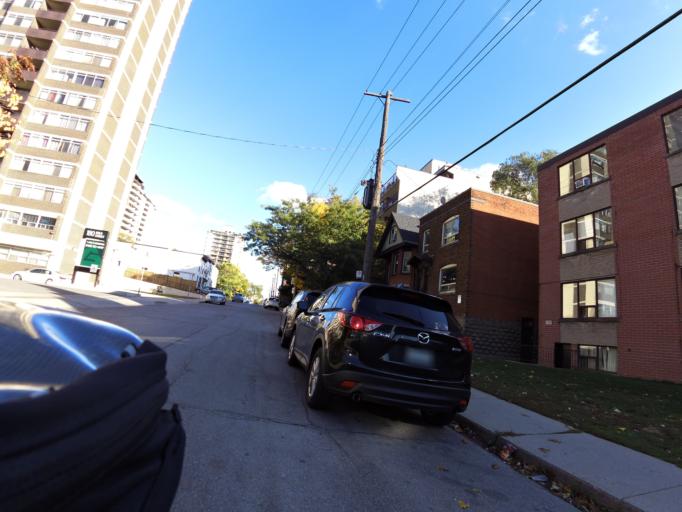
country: CA
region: Ontario
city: Hamilton
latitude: 43.2546
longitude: -79.8788
